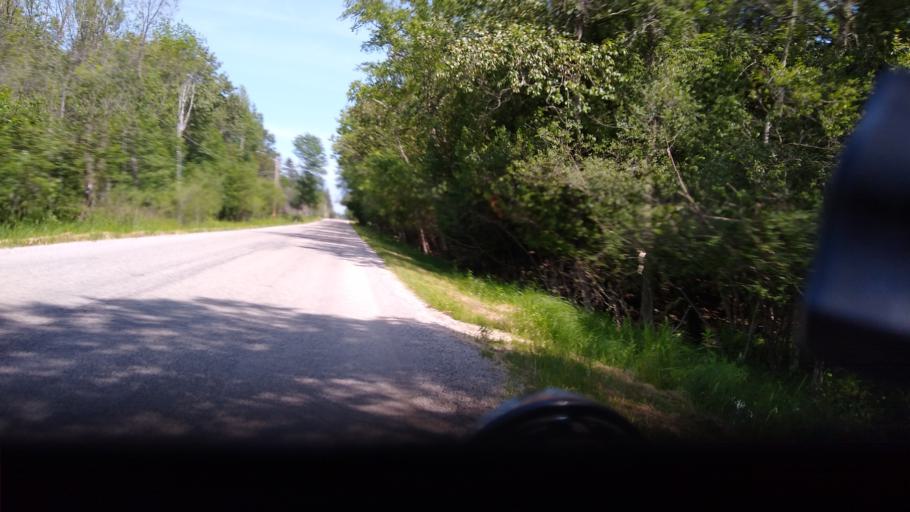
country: US
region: Michigan
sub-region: Delta County
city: Escanaba
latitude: 45.7101
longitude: -87.1360
